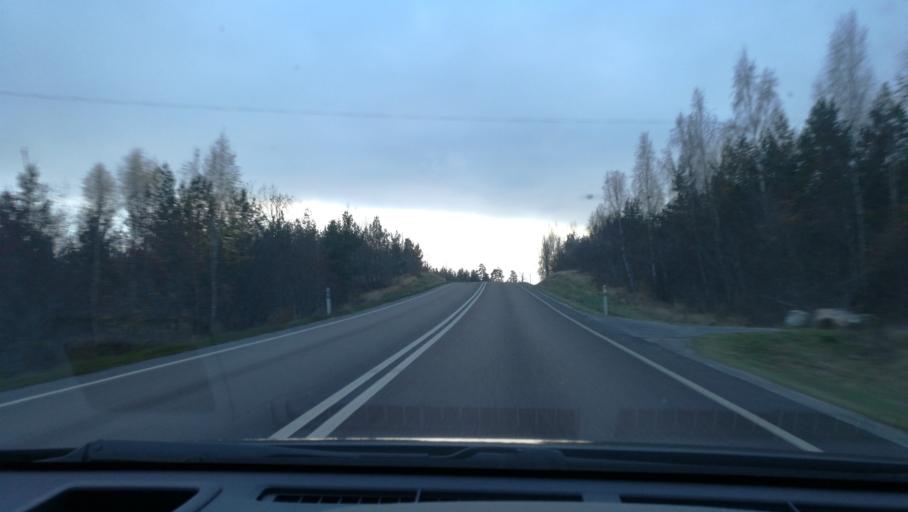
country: SE
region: Vaestmanland
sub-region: Kungsors Kommun
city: Kungsoer
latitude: 59.2604
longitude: 16.1177
